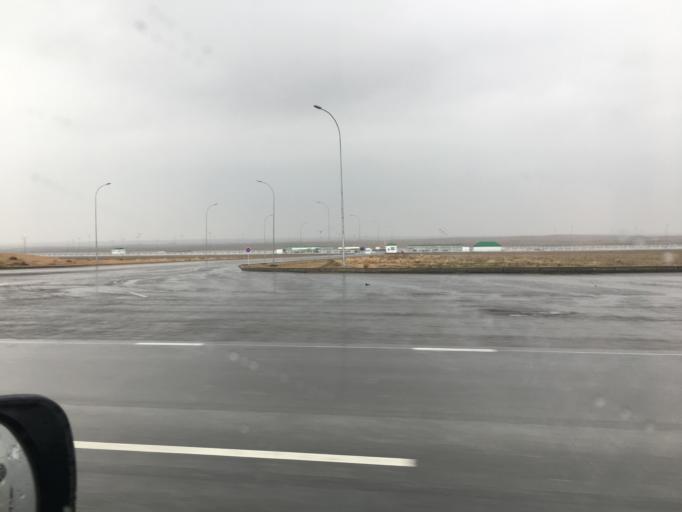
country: TM
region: Ahal
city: Annau
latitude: 37.8860
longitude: 58.6238
